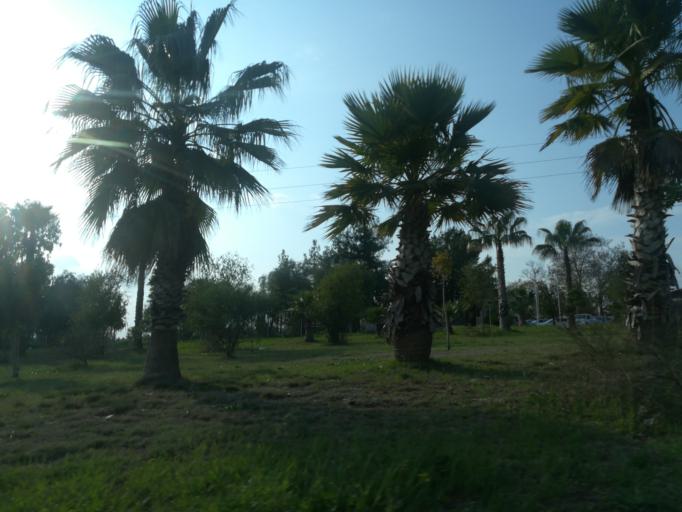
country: TR
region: Adana
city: Adana
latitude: 37.0496
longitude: 35.3568
